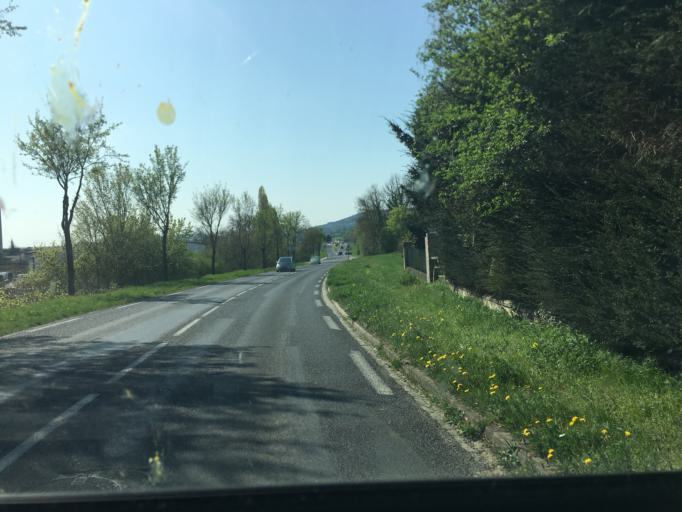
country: FR
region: Lorraine
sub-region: Departement de Meurthe-et-Moselle
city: Norroy-les-Pont-a-Mousson
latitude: 48.9220
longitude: 6.0382
